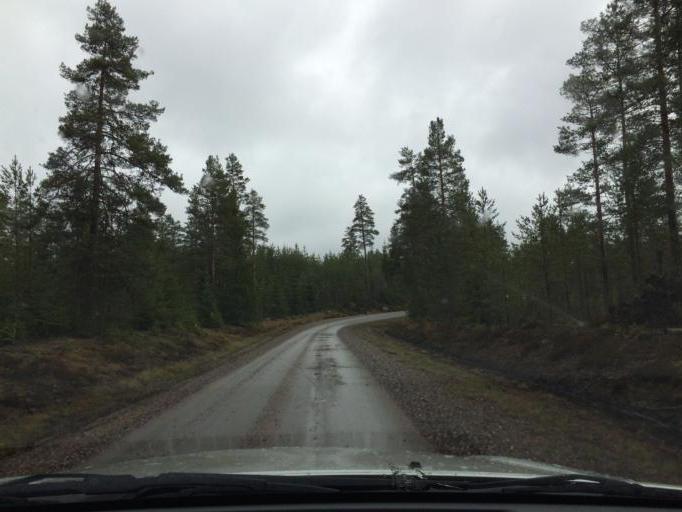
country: SE
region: OErebro
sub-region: Hallefors Kommun
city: Haellefors
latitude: 60.0281
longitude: 14.5562
